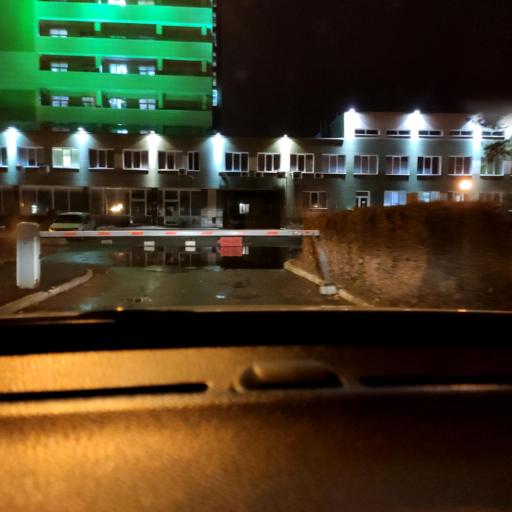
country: RU
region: Voronezj
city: Somovo
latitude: 51.6872
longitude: 39.2860
